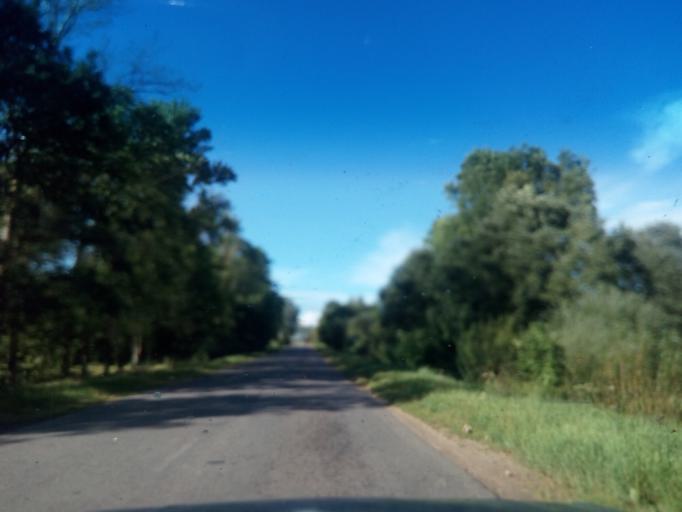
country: BY
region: Vitebsk
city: Dzisna
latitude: 55.6632
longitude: 28.3255
